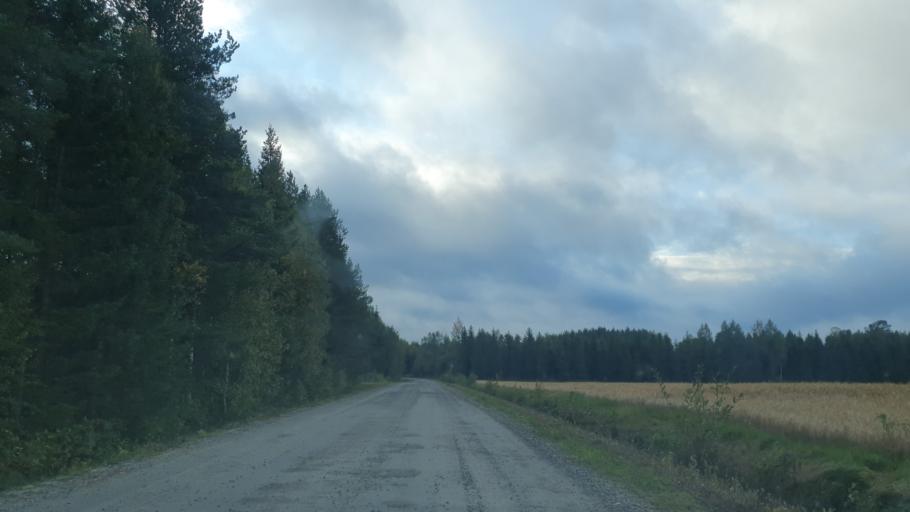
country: FI
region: Kainuu
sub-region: Kehys-Kainuu
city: Kuhmo
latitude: 64.1335
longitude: 29.5821
